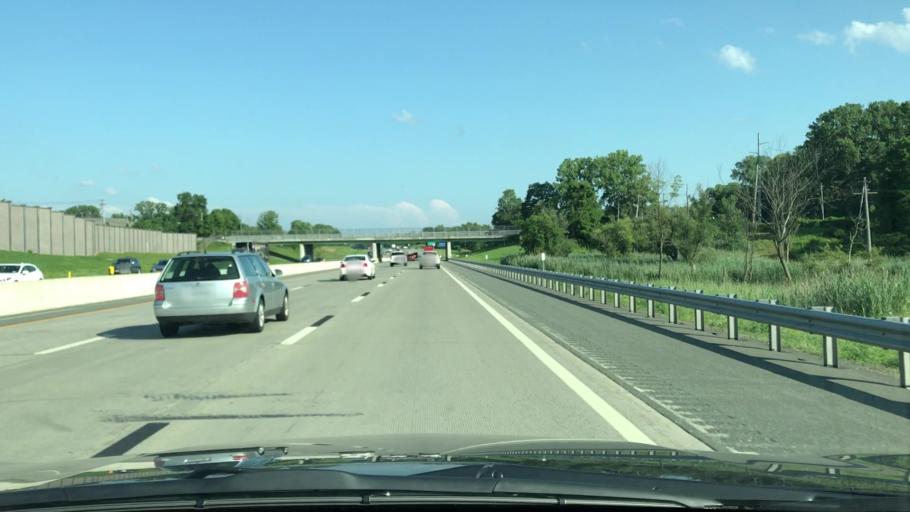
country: US
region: New York
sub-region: Albany County
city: Delmar
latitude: 42.6554
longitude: -73.8211
